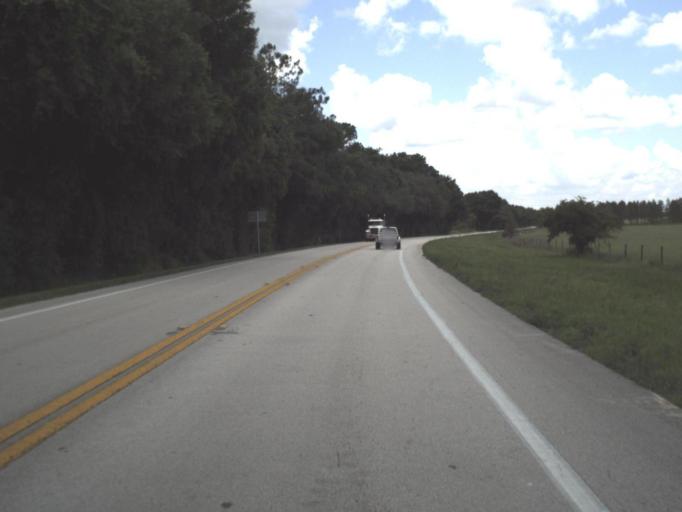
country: US
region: Florida
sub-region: Putnam County
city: Palatka
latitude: 29.5270
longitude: -81.6391
